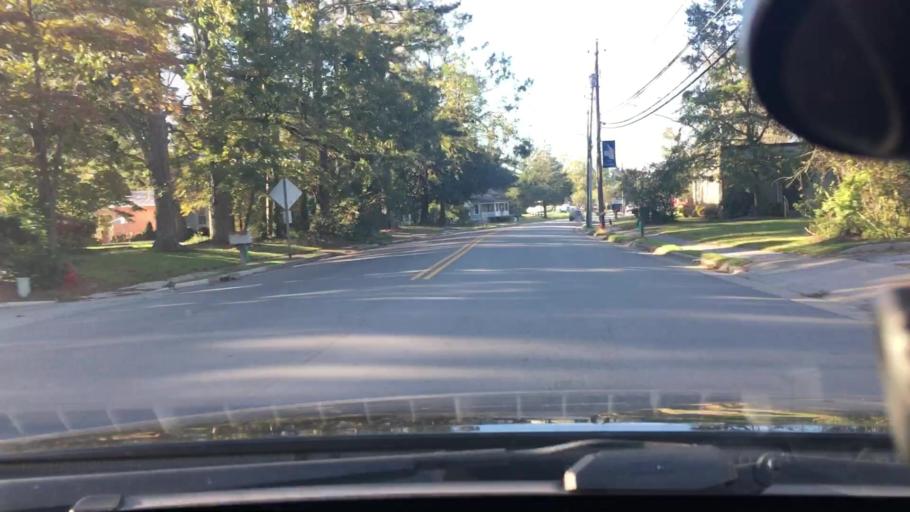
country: US
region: North Carolina
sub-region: Craven County
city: Vanceboro
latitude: 35.3014
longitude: -77.1538
